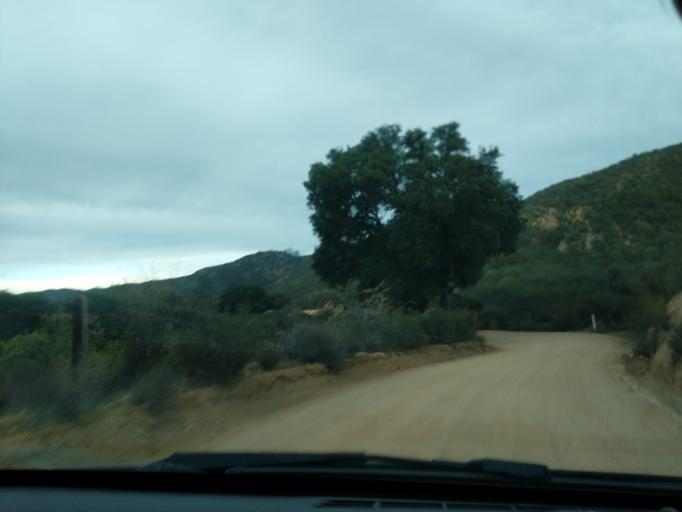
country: US
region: California
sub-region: Monterey County
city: Soledad
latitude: 36.5654
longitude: -121.2132
